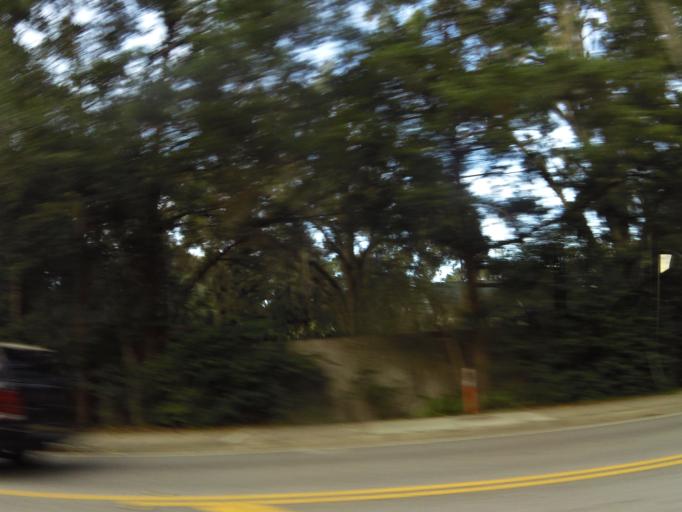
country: US
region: Florida
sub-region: Saint Johns County
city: Fruit Cove
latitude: 30.1598
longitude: -81.6202
